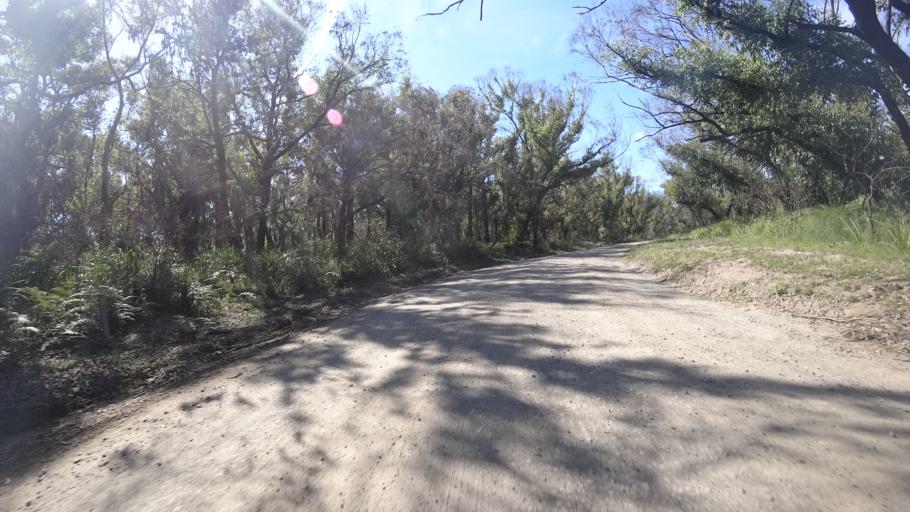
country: AU
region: New South Wales
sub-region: Shoalhaven Shire
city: Falls Creek
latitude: -35.1541
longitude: 150.7127
